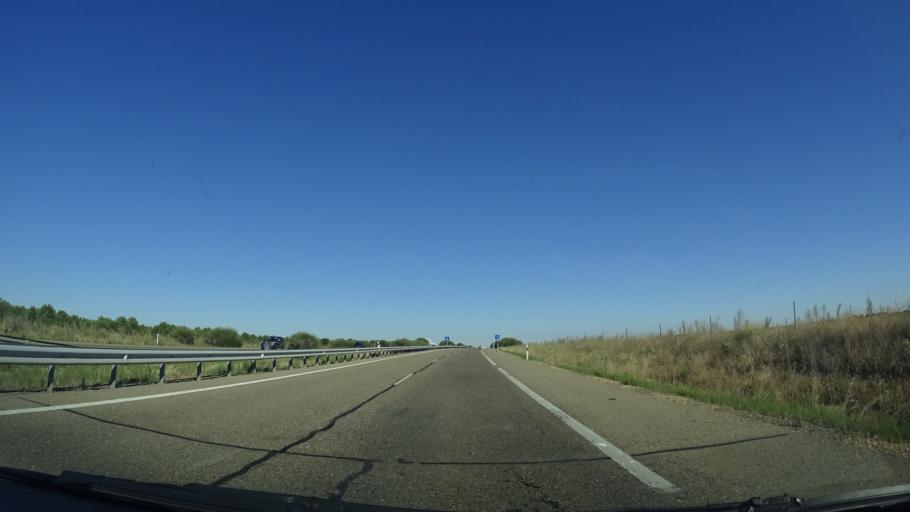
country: ES
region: Castille and Leon
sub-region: Provincia de Zamora
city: Quintanilla del Monte
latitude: 41.8210
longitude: -5.3703
